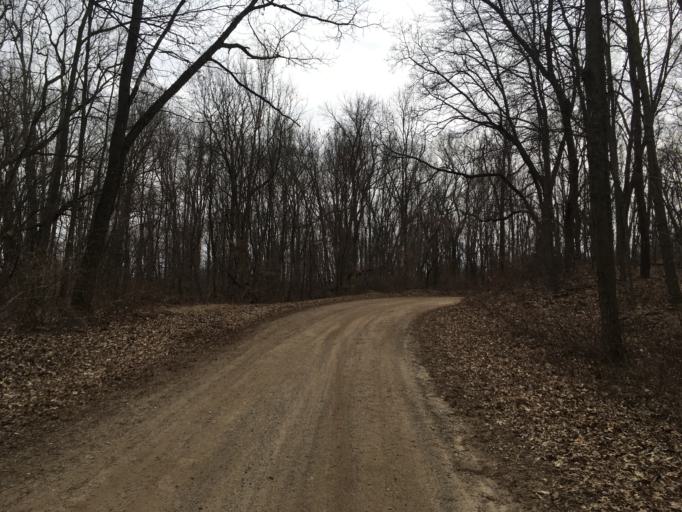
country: US
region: Michigan
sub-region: Jackson County
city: Grass Lake
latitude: 42.3214
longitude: -84.1950
